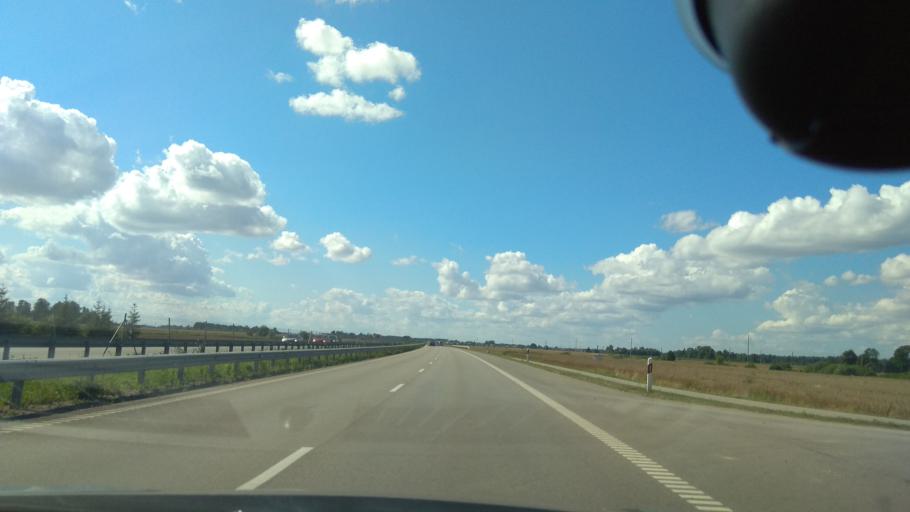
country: LT
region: Siauliu apskritis
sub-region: Siauliai
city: Siauliai
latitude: 55.9714
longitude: 23.1833
